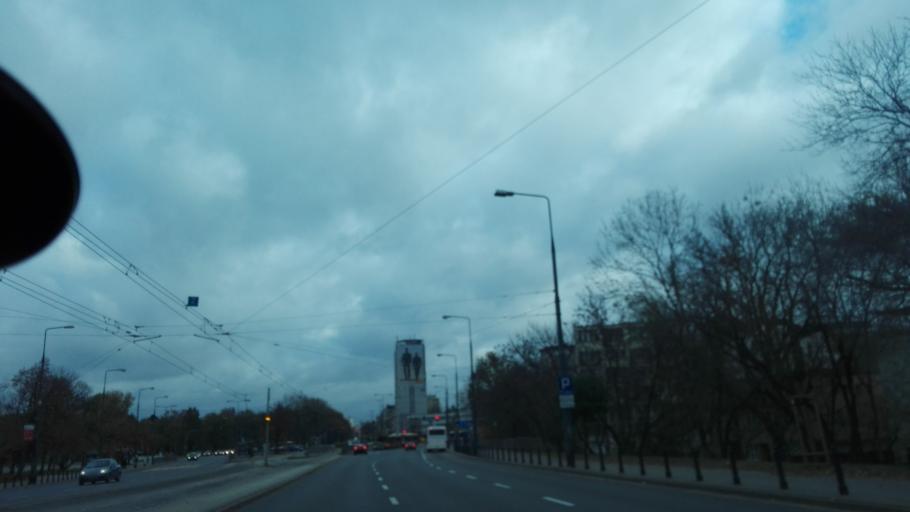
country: PL
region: Masovian Voivodeship
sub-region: Warszawa
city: Praga Polnoc
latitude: 52.2374
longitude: 21.0485
